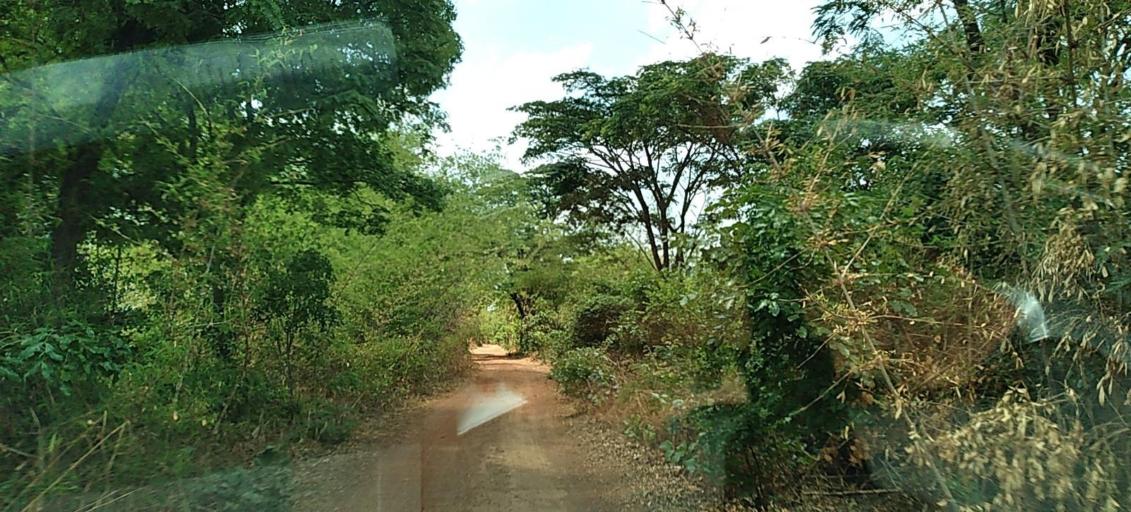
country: ZM
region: Copperbelt
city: Chingola
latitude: -12.5388
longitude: 27.6325
